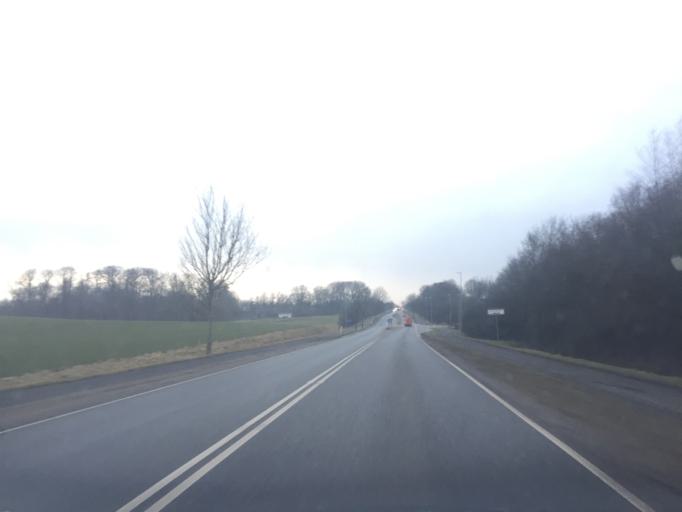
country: DK
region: Zealand
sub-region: Solrod Kommune
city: Solrod Strand
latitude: 55.5643
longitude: 12.2245
